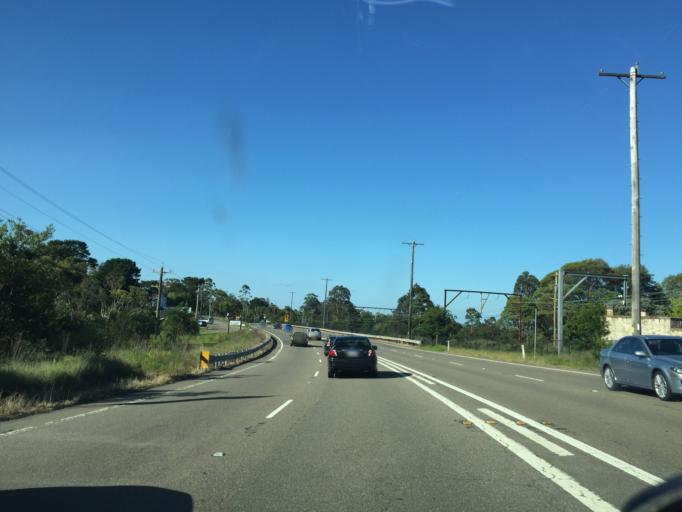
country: AU
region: New South Wales
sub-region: Blue Mountains Municipality
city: Hazelbrook
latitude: -33.7104
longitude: 150.5229
